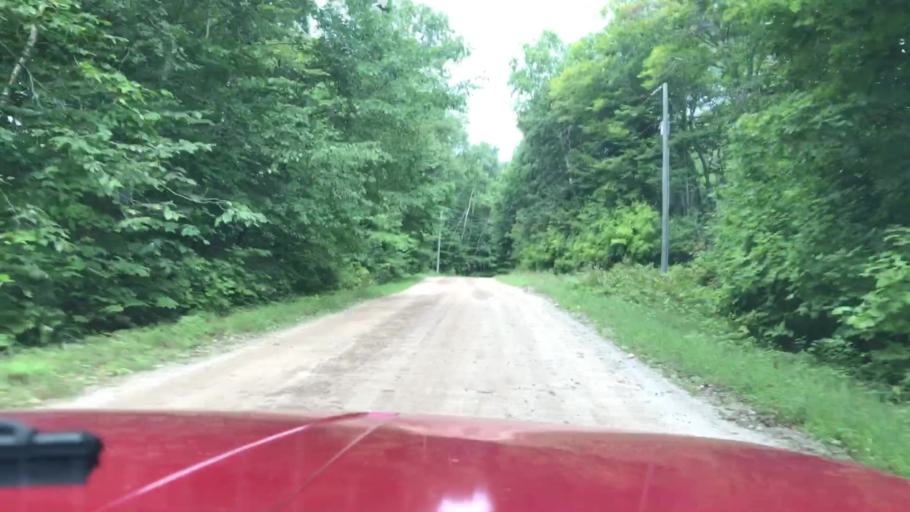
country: US
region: Michigan
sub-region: Charlevoix County
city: Charlevoix
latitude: 45.7266
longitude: -85.5653
